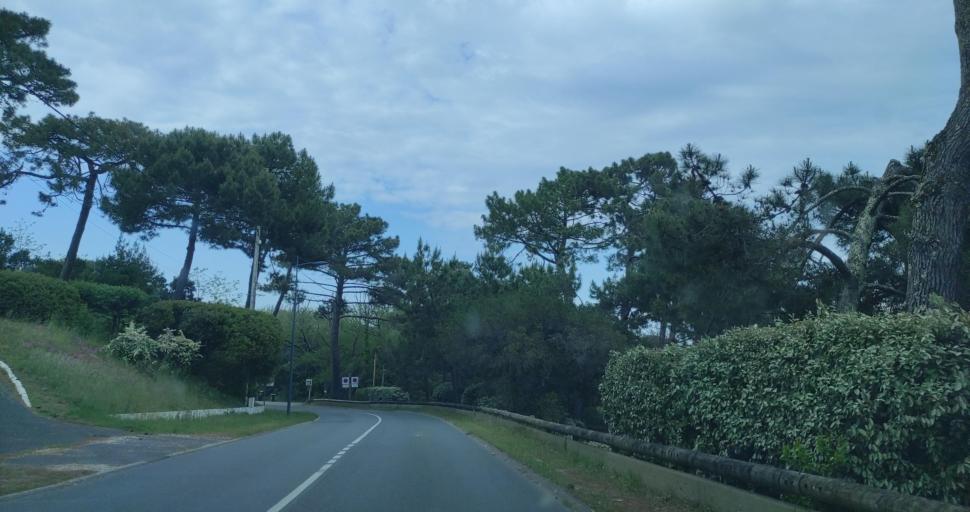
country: FR
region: Aquitaine
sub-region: Departement de la Gironde
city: Arcachon
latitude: 44.6706
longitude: -1.2408
